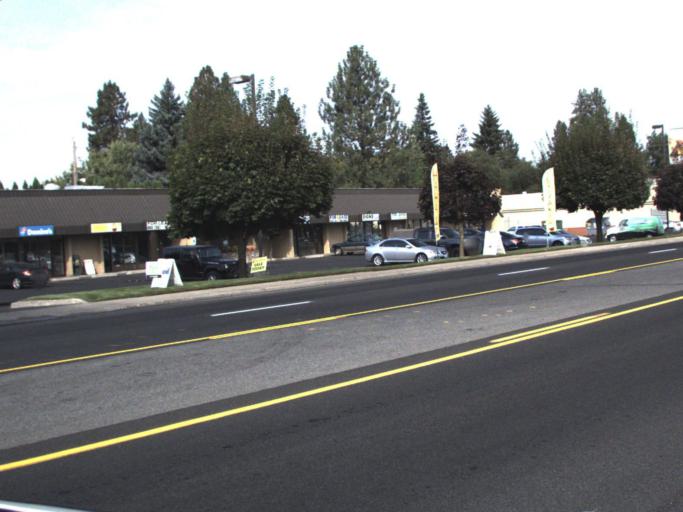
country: US
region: Washington
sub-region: Spokane County
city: Country Homes
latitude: 47.7424
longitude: -117.4114
